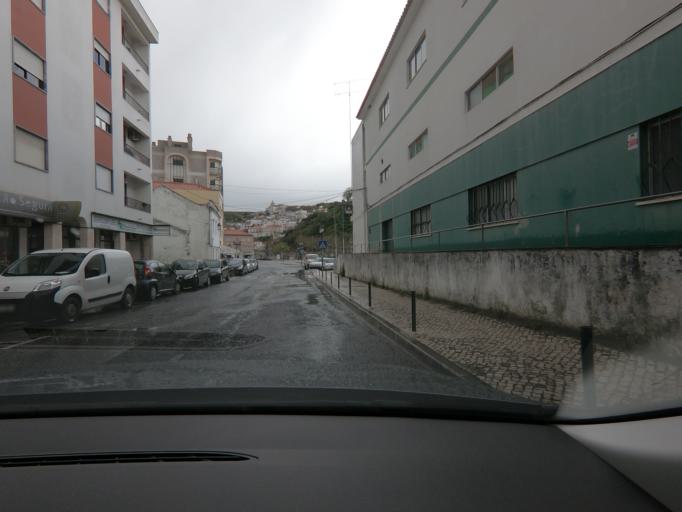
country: PT
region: Lisbon
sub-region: Alenquer
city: Alenquer
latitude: 39.0565
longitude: -9.0058
